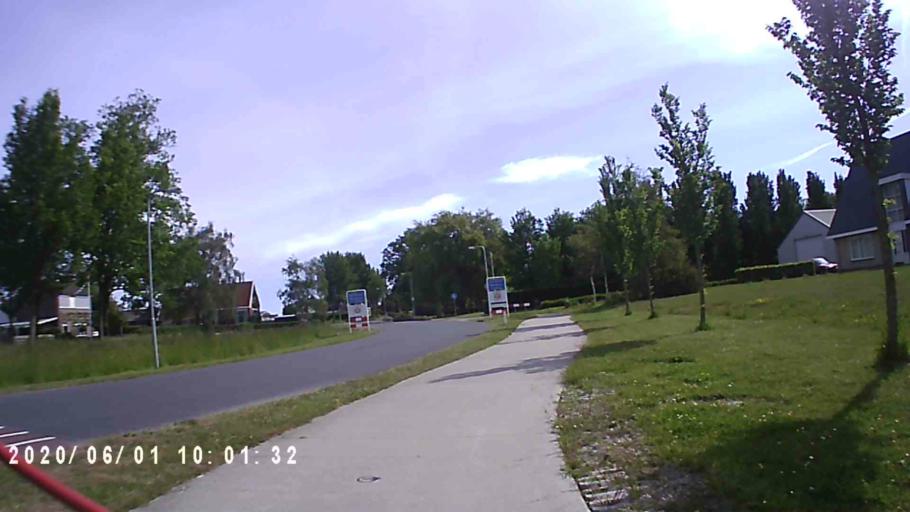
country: NL
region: Friesland
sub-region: Menameradiel
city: Berltsum
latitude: 53.2392
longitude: 5.6372
